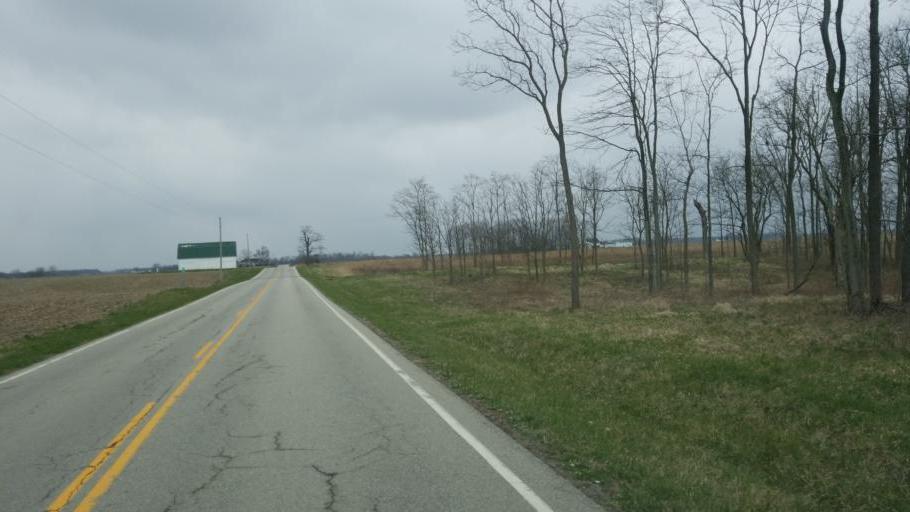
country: US
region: Ohio
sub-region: Union County
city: Richwood
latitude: 40.4358
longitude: -83.3854
